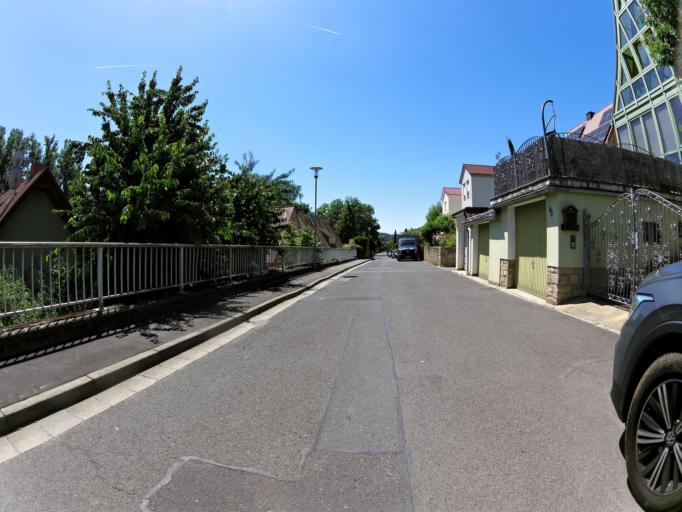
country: DE
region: Bavaria
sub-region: Regierungsbezirk Unterfranken
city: Frickenhausen
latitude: 49.6710
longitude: 10.0850
